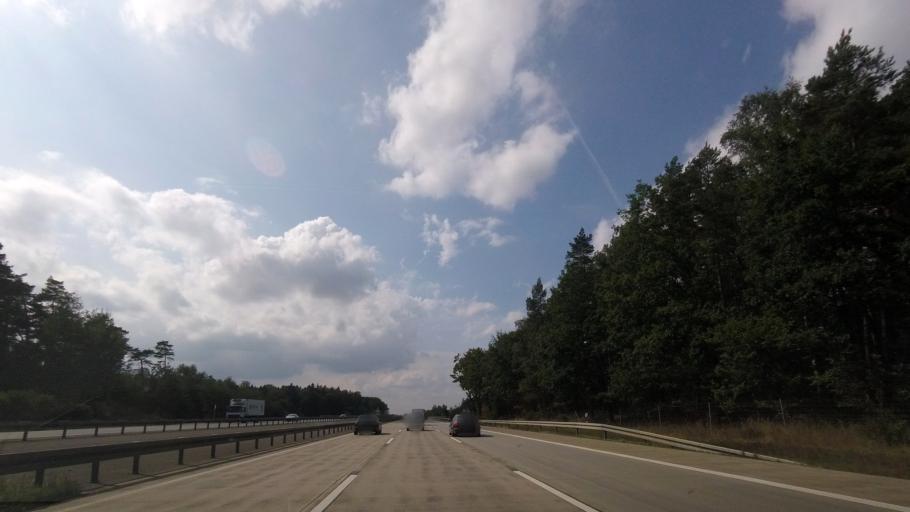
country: DE
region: Thuringia
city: Schleifreisen
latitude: 50.8779
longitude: 11.8217
